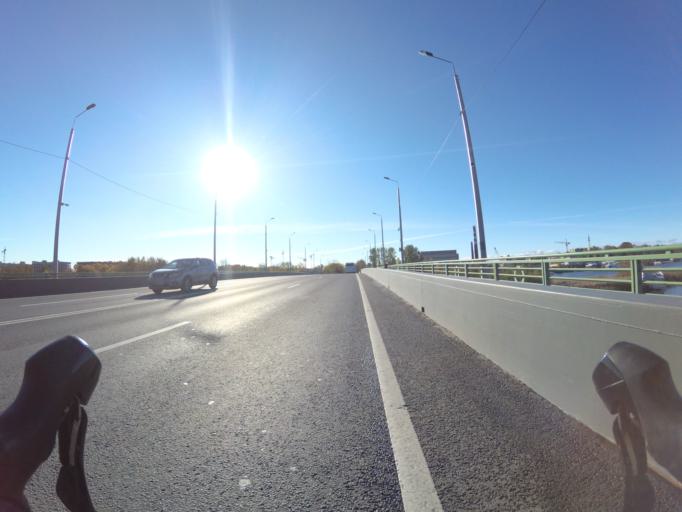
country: RU
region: Leningrad
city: Krestovskiy ostrov
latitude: 59.9659
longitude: 30.2553
